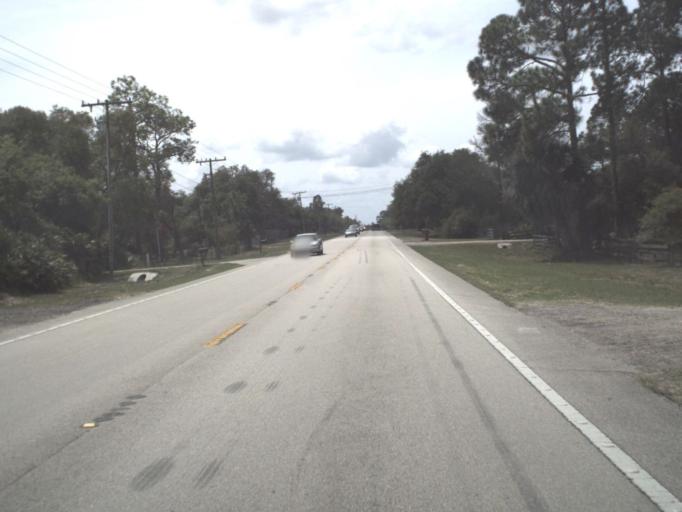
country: US
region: Florida
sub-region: Lake County
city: Lake Mack-Forest Hills
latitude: 28.9681
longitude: -81.4100
